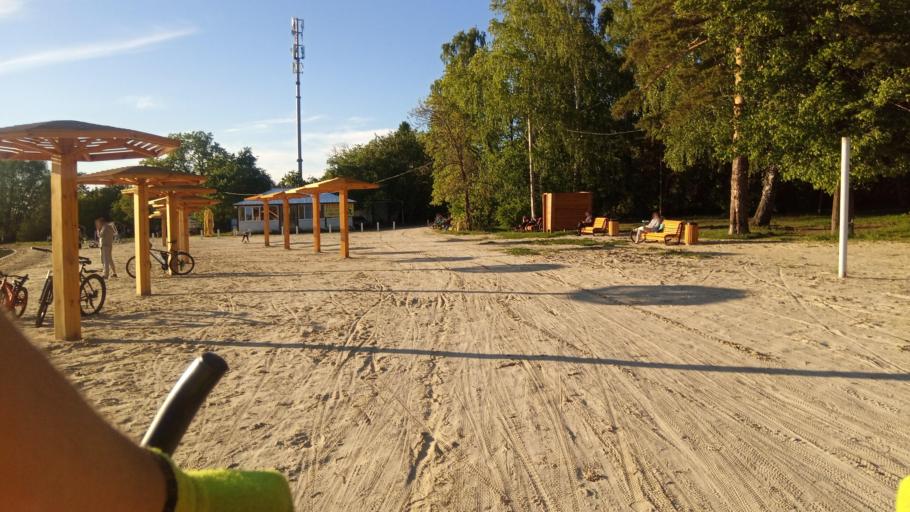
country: RU
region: Chelyabinsk
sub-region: Gorod Chelyabinsk
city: Chelyabinsk
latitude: 55.1452
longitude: 61.3295
